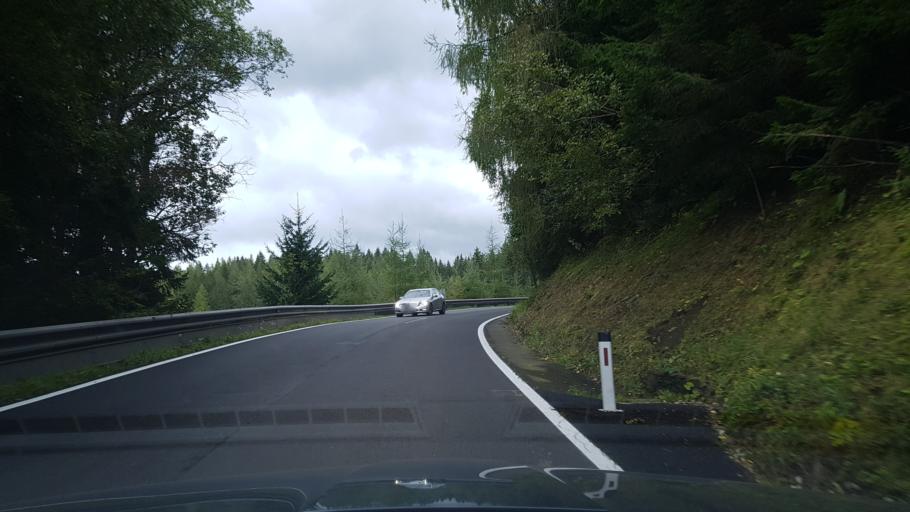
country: AT
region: Styria
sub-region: Politischer Bezirk Murtal
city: Kleinlobming
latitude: 47.1343
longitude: 14.8673
